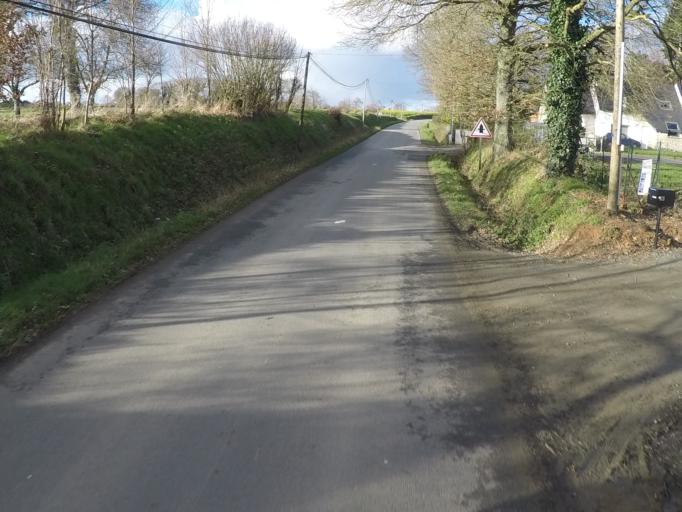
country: FR
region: Brittany
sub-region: Departement des Cotes-d'Armor
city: Plouagat
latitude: 48.5562
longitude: -2.9800
